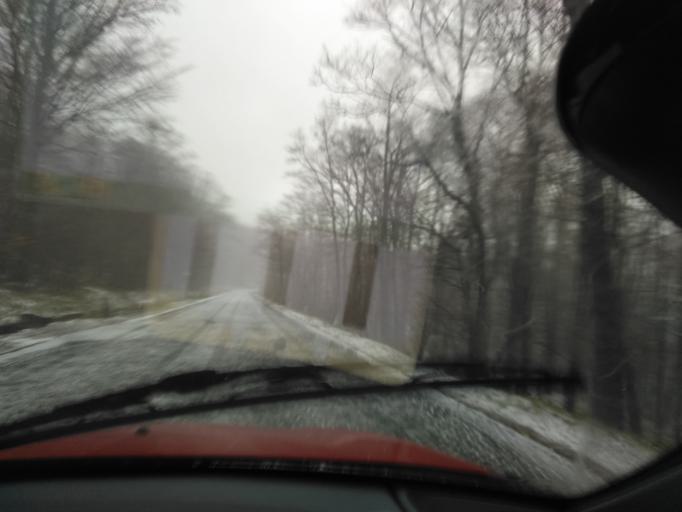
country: AT
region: Lower Austria
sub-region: Politischer Bezirk Wien-Umgebung
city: Klosterneuburg
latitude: 48.2589
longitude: 16.2914
